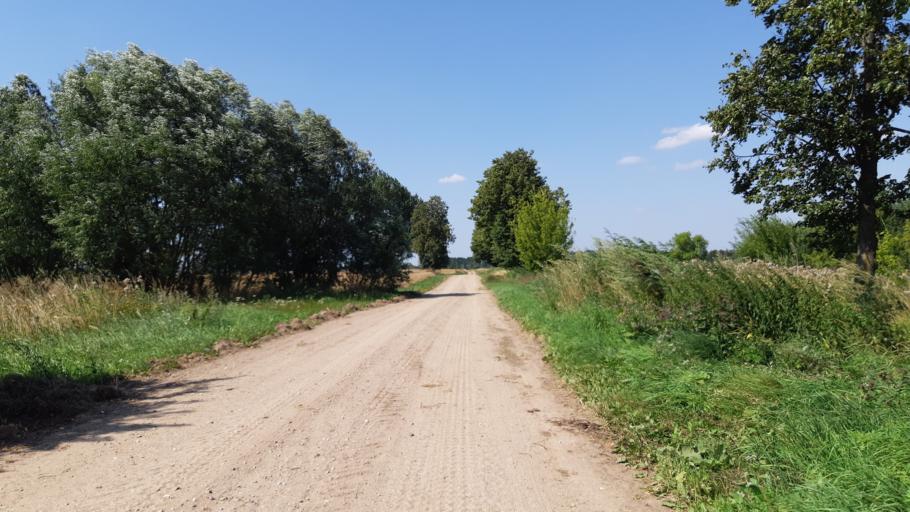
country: LT
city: Virbalis
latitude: 54.6386
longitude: 22.8224
